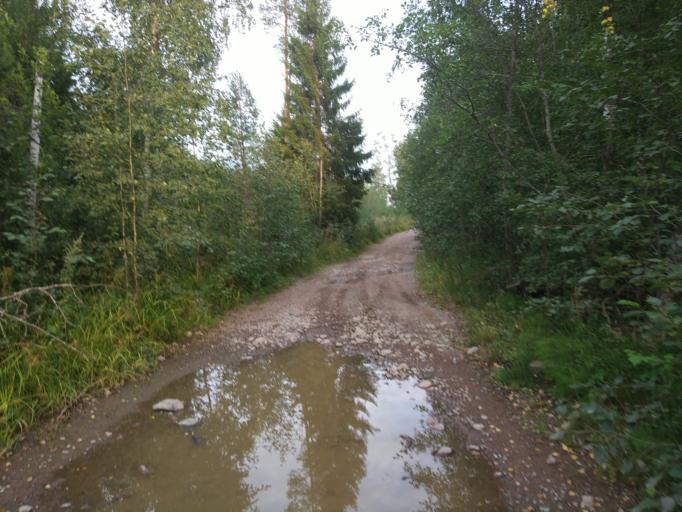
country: RU
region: Leningrad
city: Kuznechnoye
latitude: 61.1159
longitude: 29.6047
